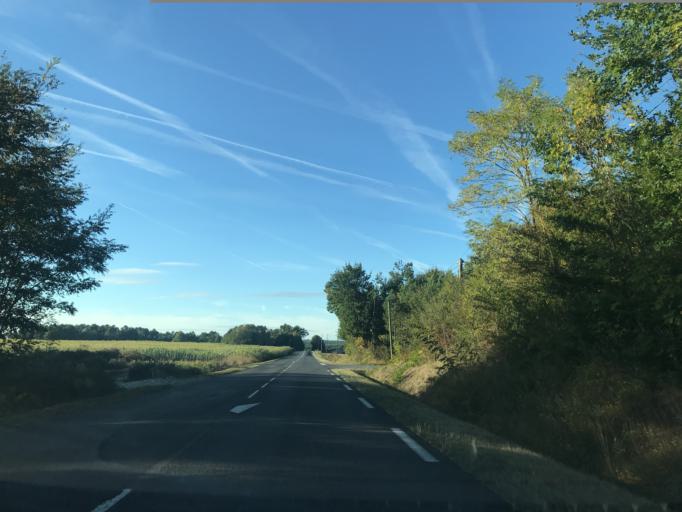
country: FR
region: Poitou-Charentes
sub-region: Departement de la Charente-Maritime
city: Montguyon
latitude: 45.1982
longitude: -0.1444
